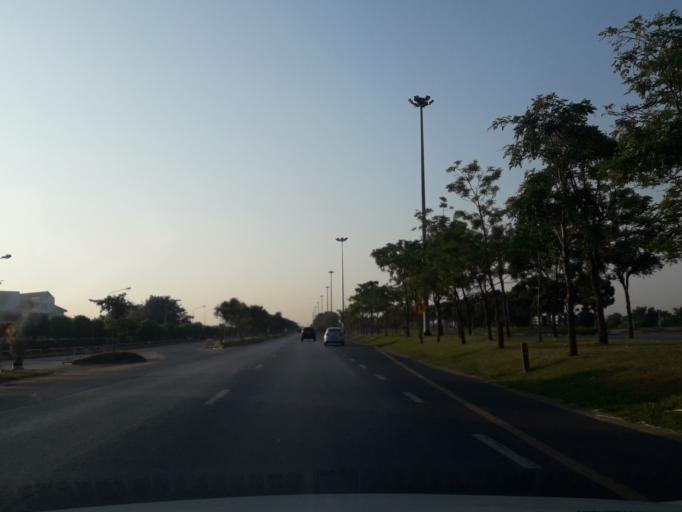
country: TH
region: Phra Nakhon Si Ayutthaya
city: Bang Pa-in
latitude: 14.2177
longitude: 100.5431
